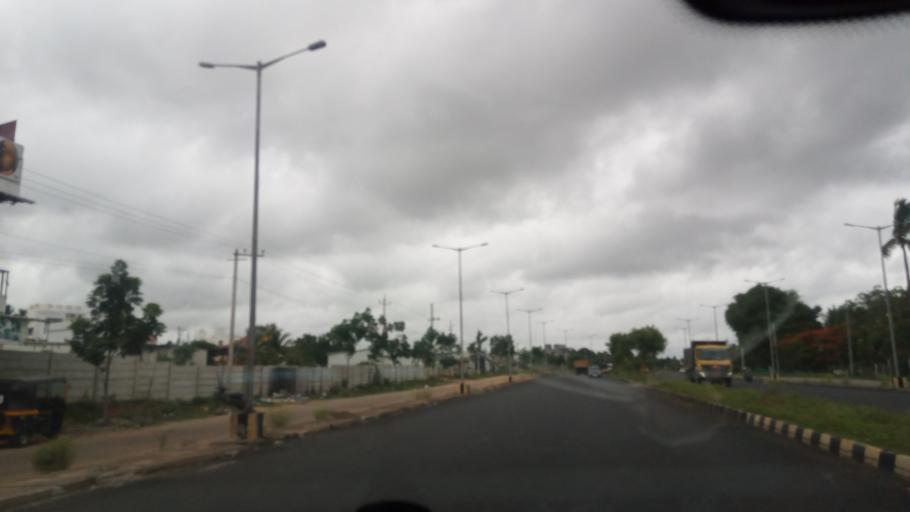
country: IN
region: Karnataka
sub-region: Mysore
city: Mysore
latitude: 12.2965
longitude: 76.6035
